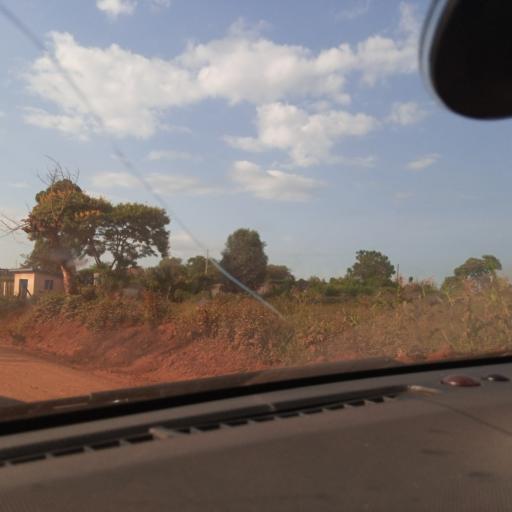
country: UG
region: Central Region
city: Masaka
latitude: -0.3593
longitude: 31.7448
